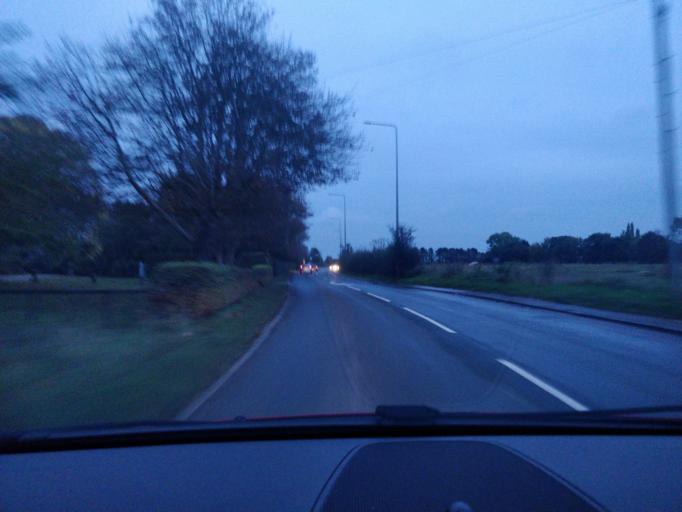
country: GB
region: England
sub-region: Lancashire
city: Ormskirk
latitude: 53.5861
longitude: -2.9120
